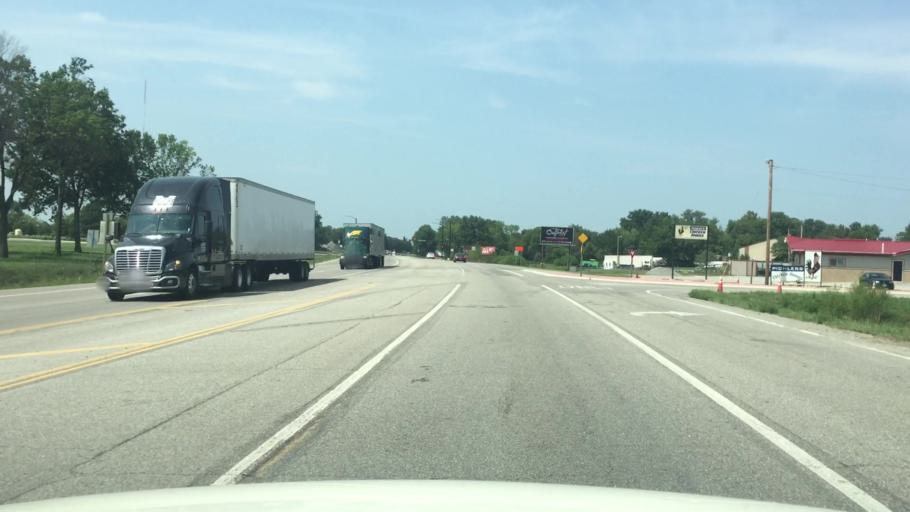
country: US
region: Kansas
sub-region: Crawford County
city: Pittsburg
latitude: 37.3428
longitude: -94.7058
